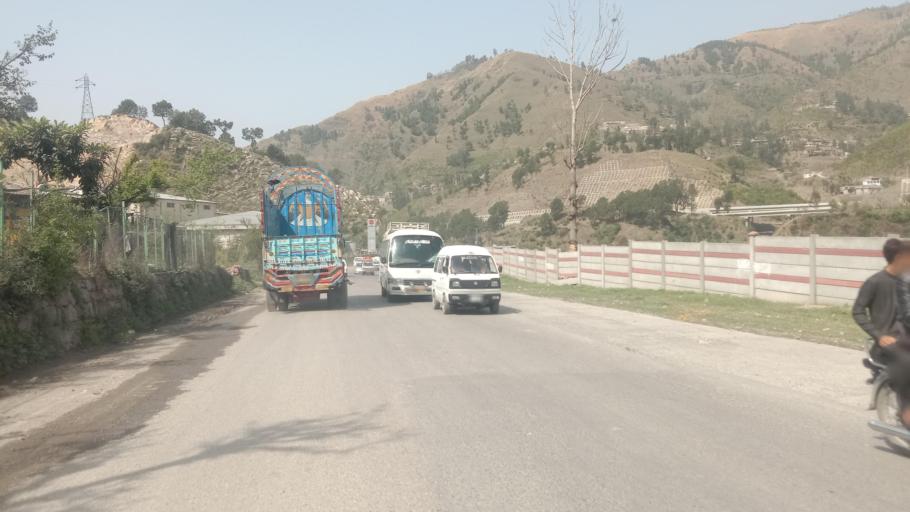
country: PK
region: Khyber Pakhtunkhwa
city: Abbottabad
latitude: 34.1235
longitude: 73.1908
